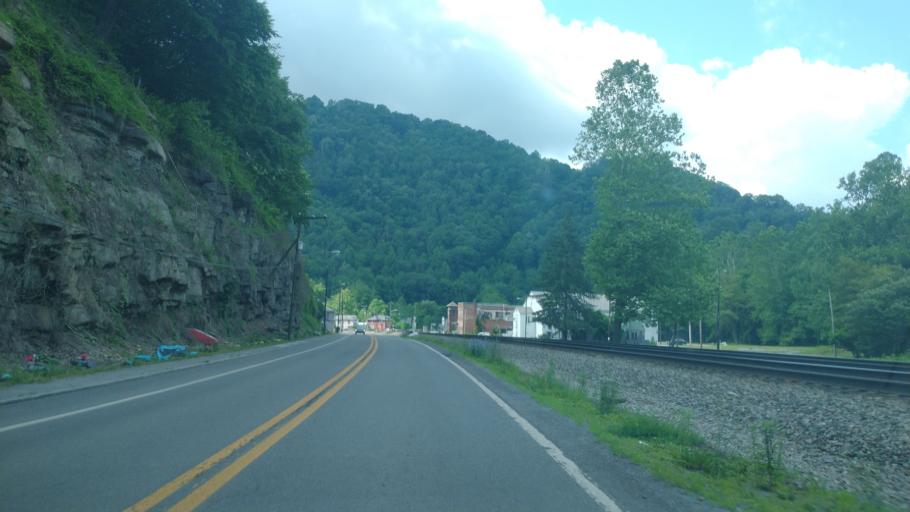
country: US
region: West Virginia
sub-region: McDowell County
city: Welch
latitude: 37.4190
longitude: -81.4438
